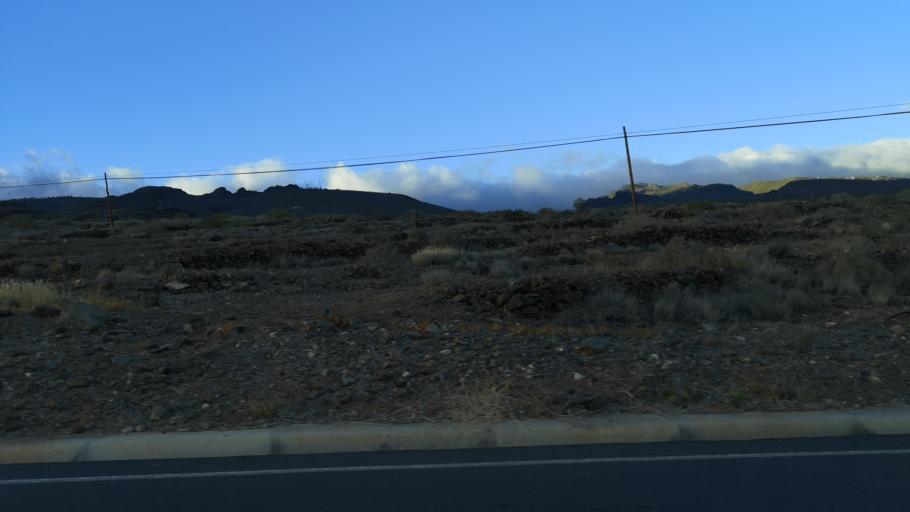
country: ES
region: Canary Islands
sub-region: Provincia de Santa Cruz de Tenerife
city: Alajero
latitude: 28.0338
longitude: -17.2138
